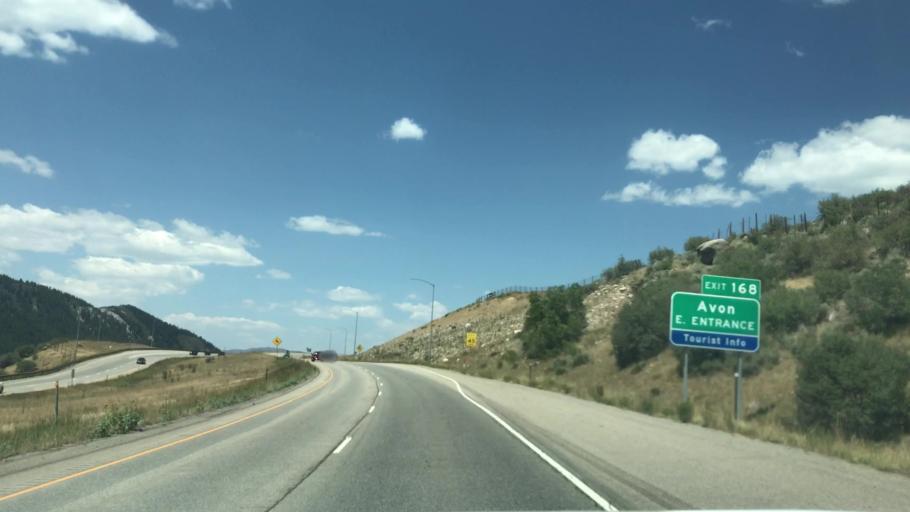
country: US
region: Colorado
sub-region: Eagle County
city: Avon
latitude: 39.6246
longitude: -106.4879
